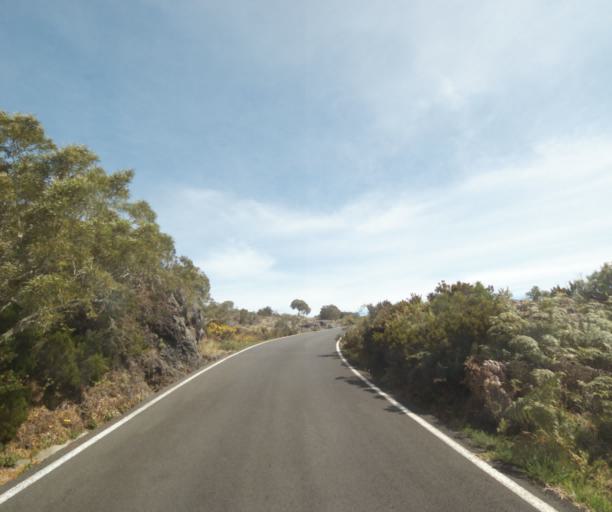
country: RE
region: Reunion
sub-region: Reunion
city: Trois-Bassins
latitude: -21.0680
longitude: 55.3786
